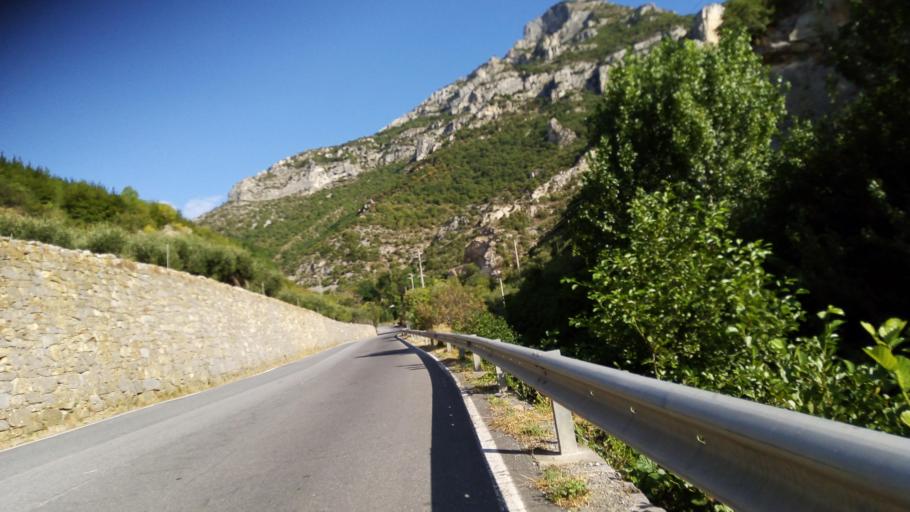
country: IT
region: Liguria
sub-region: Provincia di Savona
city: Toirano
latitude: 44.1337
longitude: 8.2003
